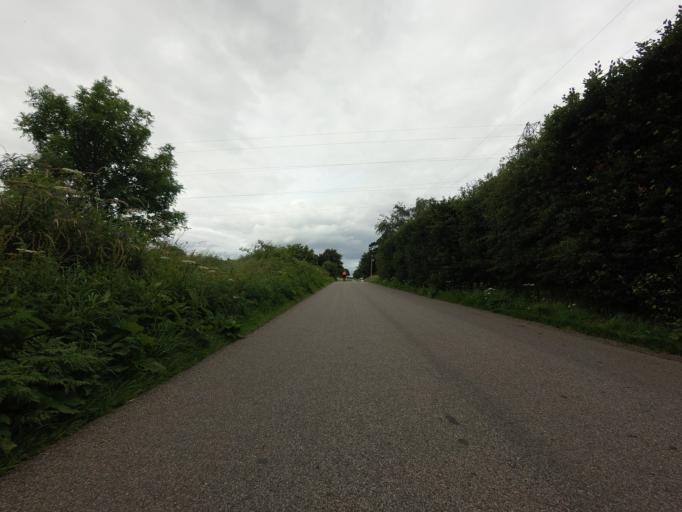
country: GB
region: Scotland
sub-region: Moray
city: Forres
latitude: 57.5989
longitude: -3.7198
